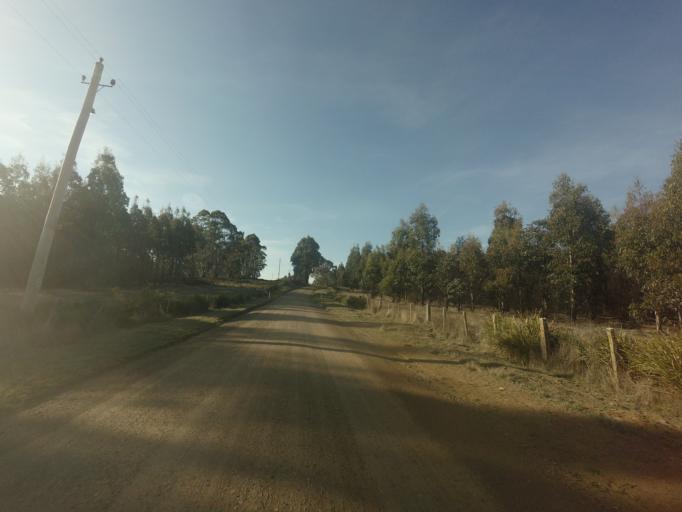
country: AU
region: Tasmania
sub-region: Brighton
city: Bridgewater
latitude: -42.4529
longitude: 147.3830
